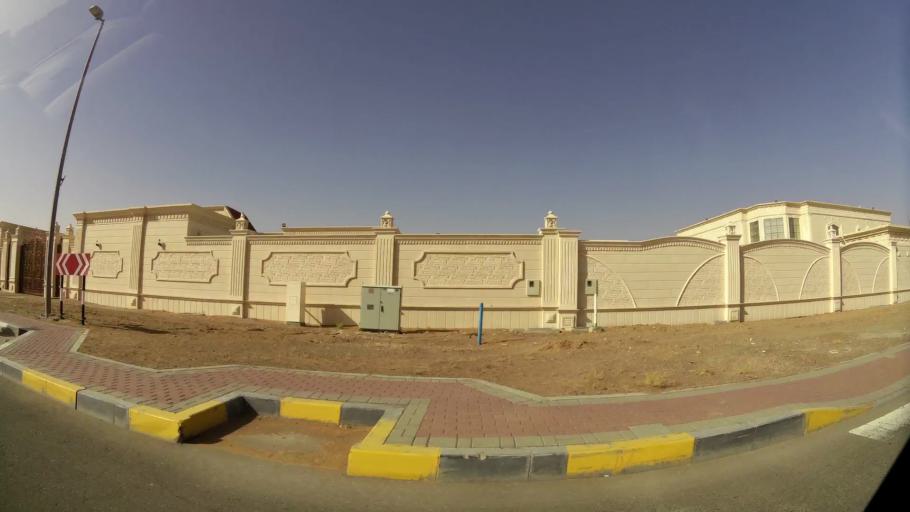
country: OM
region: Al Buraimi
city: Al Buraymi
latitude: 24.3484
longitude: 55.7996
